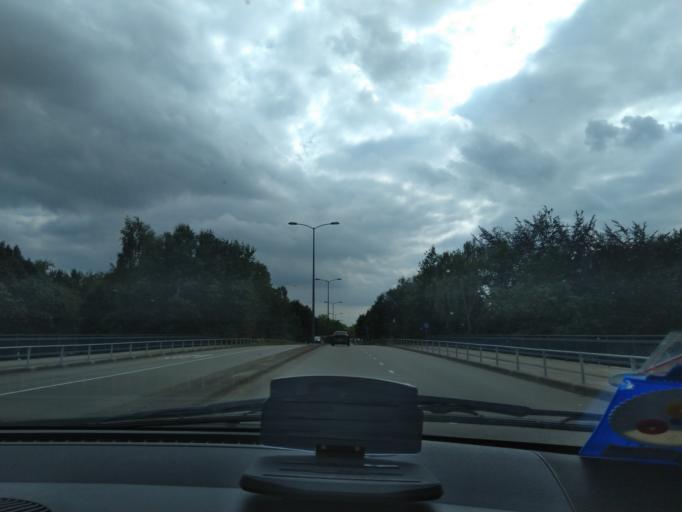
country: NL
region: North Brabant
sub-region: Gemeente Oosterhout
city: Oosterhout
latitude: 51.6324
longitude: 4.8591
